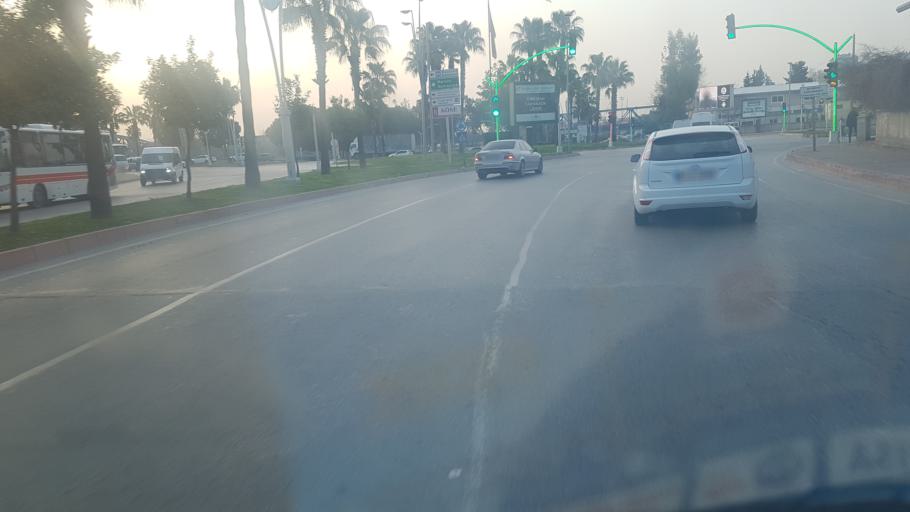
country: TR
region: Adana
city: Adana
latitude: 37.0089
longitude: 35.3318
